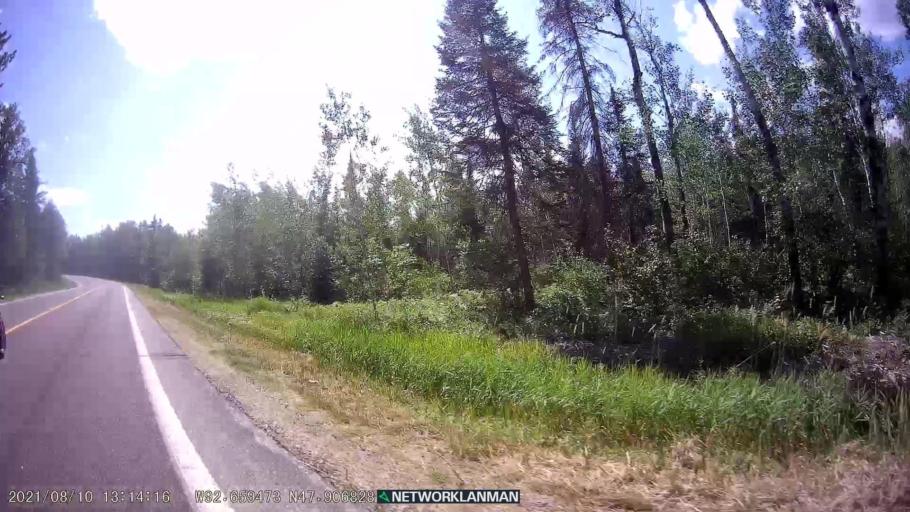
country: US
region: Minnesota
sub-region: Saint Louis County
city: Mountain Iron
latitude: 47.9066
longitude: -92.6596
